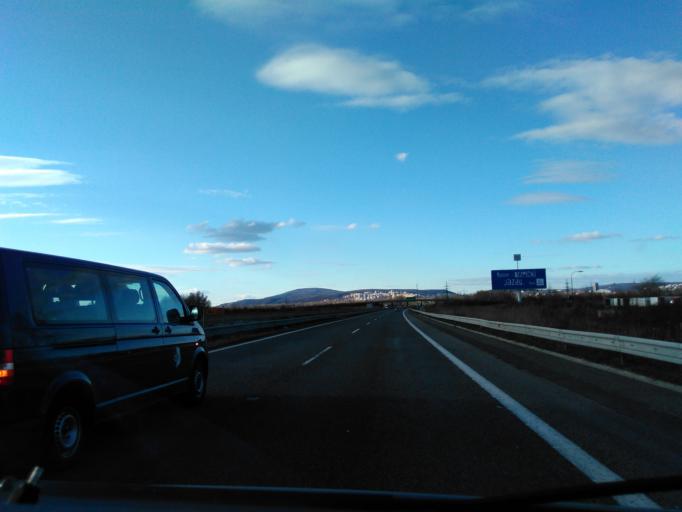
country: AT
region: Burgenland
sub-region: Politischer Bezirk Neusiedl am See
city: Kittsee
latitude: 48.1111
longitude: 17.0846
